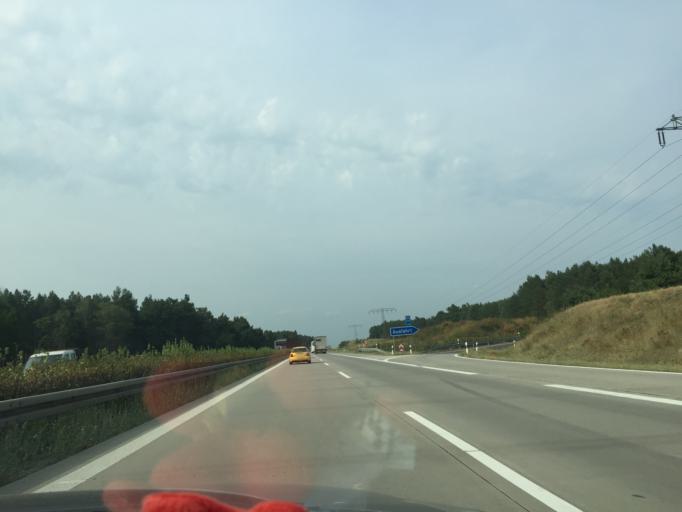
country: DE
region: Brandenburg
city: Teupitz
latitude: 52.1212
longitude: 13.6465
